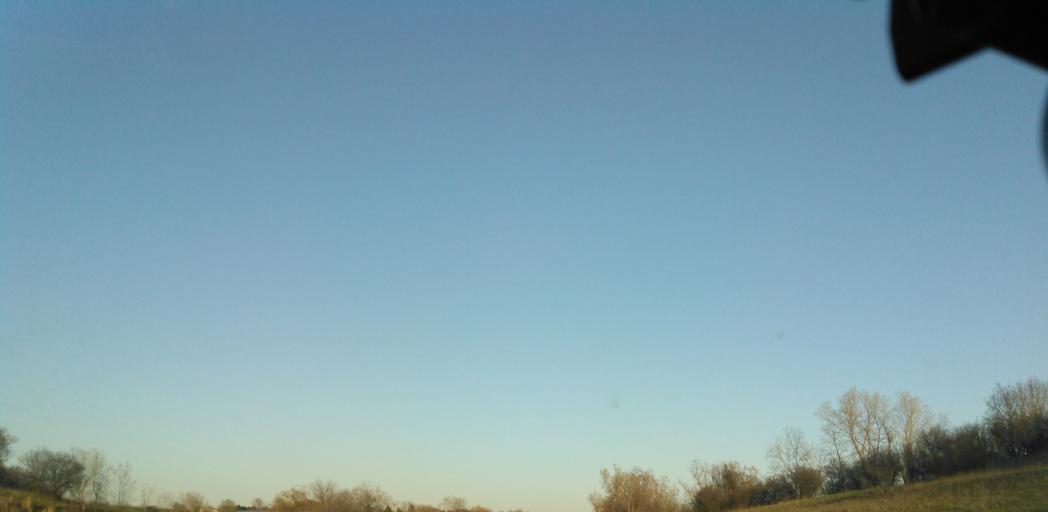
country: US
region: New York
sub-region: Monroe County
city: Pittsford
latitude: 43.0452
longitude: -77.5623
